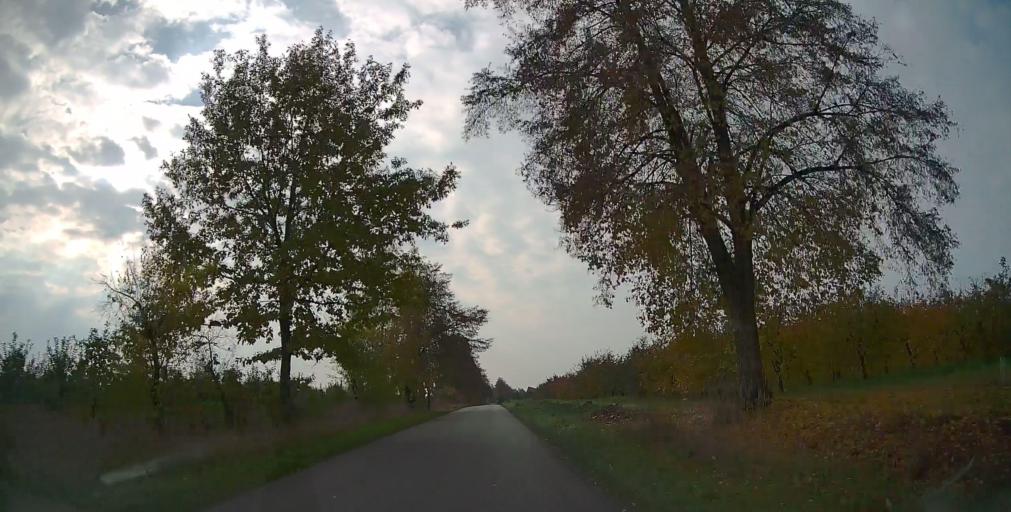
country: PL
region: Masovian Voivodeship
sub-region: Powiat grojecki
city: Mogielnica
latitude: 51.6794
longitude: 20.7145
